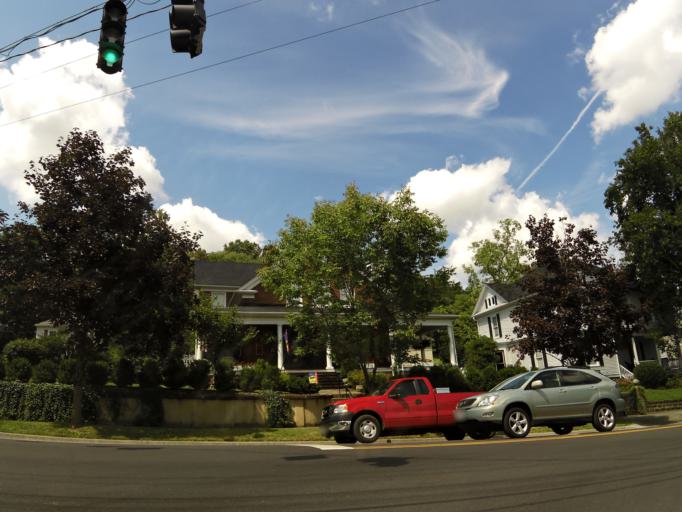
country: US
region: Virginia
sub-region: Washington County
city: Abingdon
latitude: 36.7109
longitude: -81.9778
